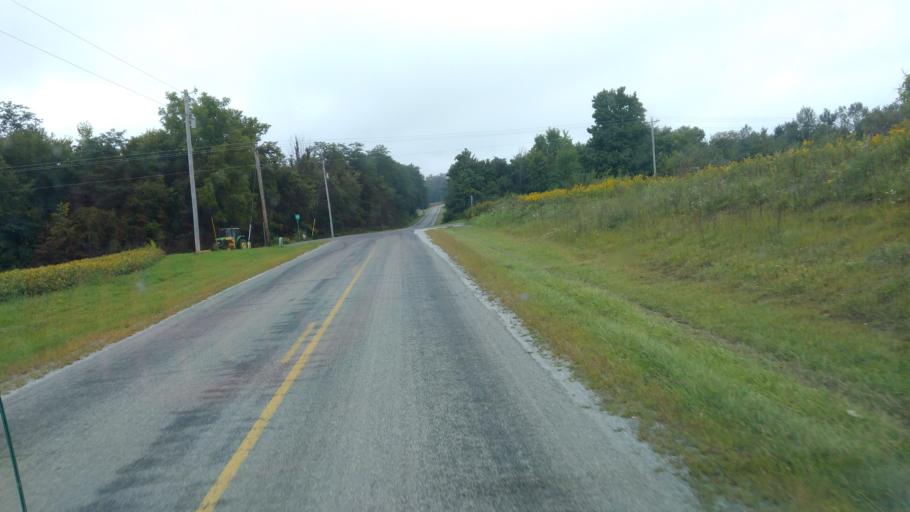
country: US
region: Ohio
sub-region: Hardin County
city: Kenton
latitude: 40.5734
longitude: -83.6331
